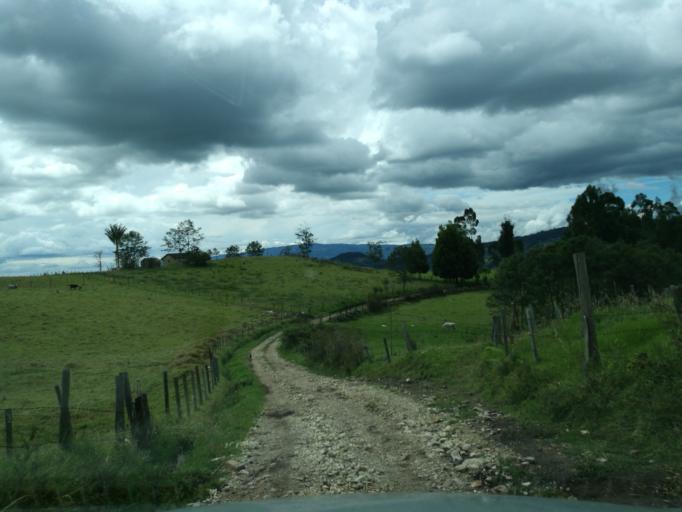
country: CO
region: Boyaca
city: Arcabuco
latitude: 5.7493
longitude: -73.4632
